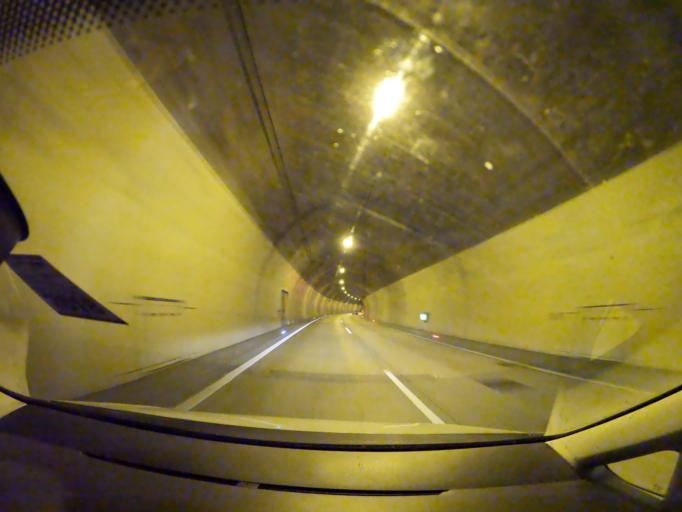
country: AT
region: Styria
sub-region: Politischer Bezirk Voitsberg
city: Edelschrott
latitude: 46.9966
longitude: 15.0663
